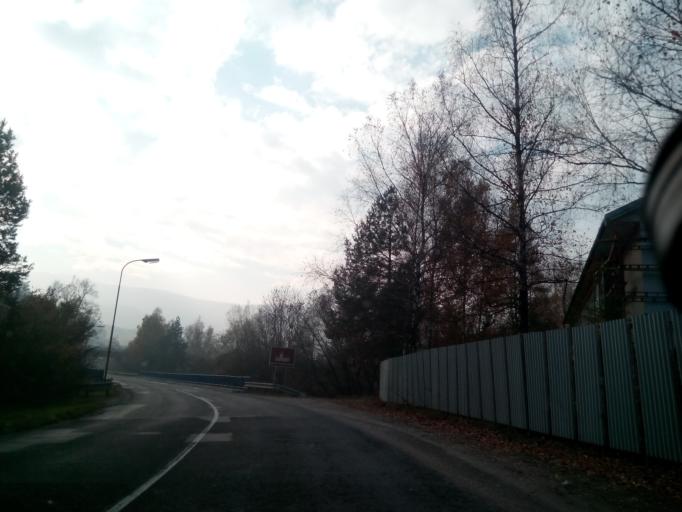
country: SK
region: Kosicky
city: Gelnica
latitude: 48.8798
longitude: 20.9975
